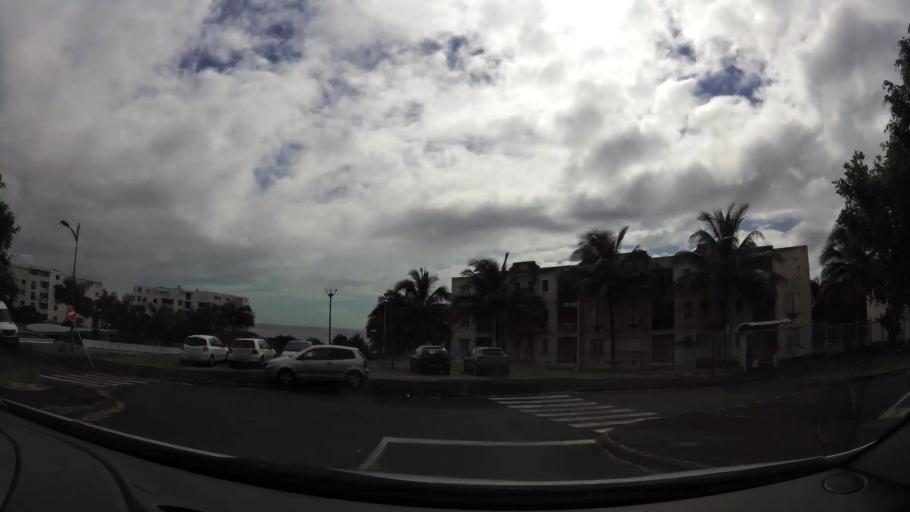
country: RE
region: Reunion
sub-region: Reunion
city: Sainte-Marie
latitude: -20.8989
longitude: 55.5555
